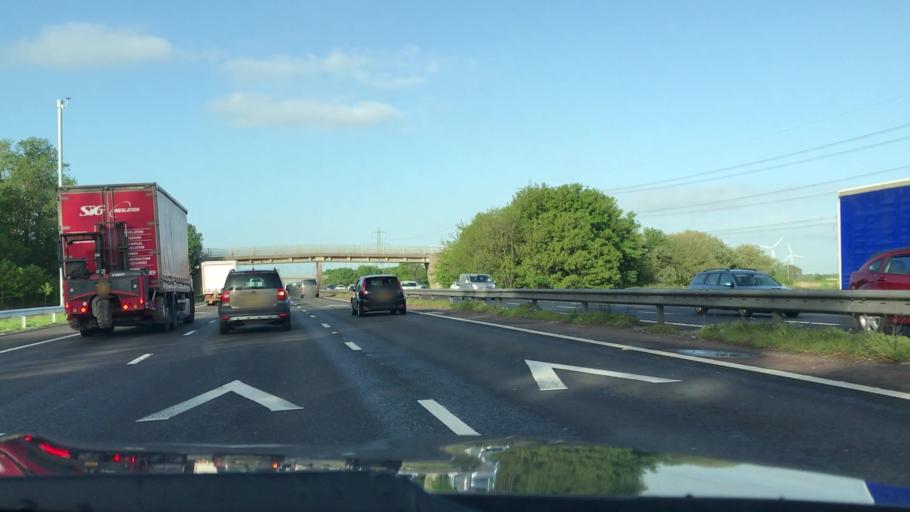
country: GB
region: England
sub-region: Cheshire West and Chester
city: Frodsham
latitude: 53.2927
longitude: -2.7418
